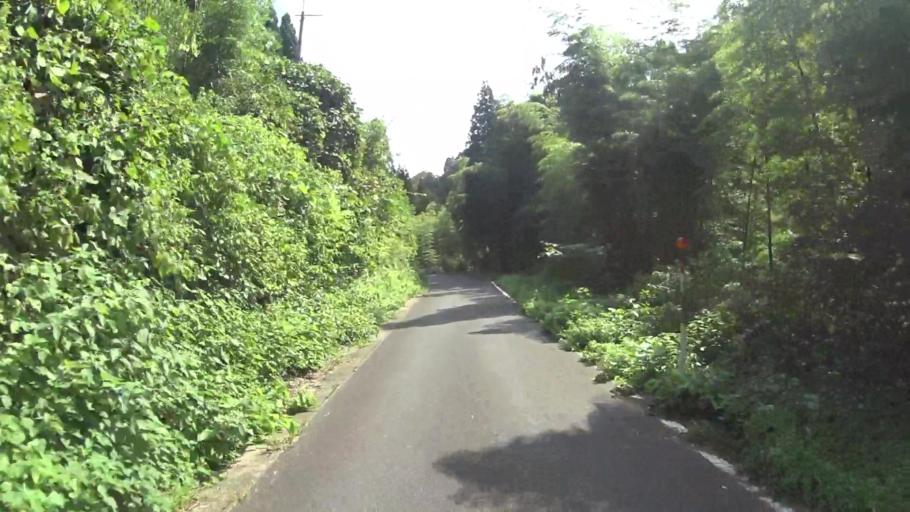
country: JP
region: Kyoto
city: Miyazu
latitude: 35.6560
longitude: 135.2519
